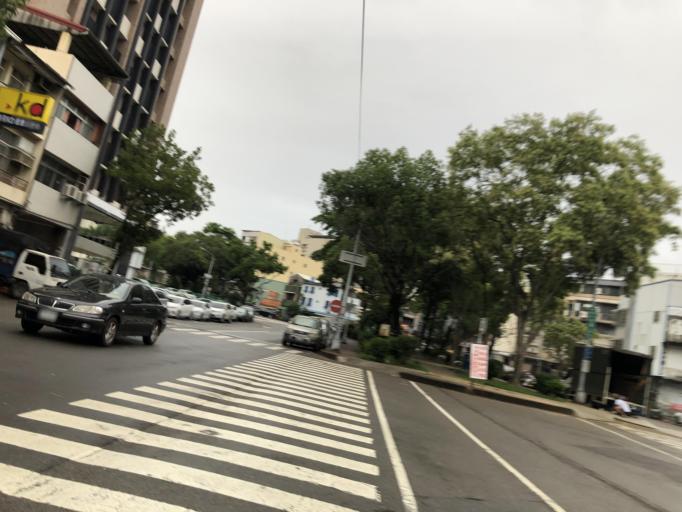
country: TW
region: Taiwan
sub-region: Taichung City
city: Taichung
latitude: 24.1516
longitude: 120.6727
